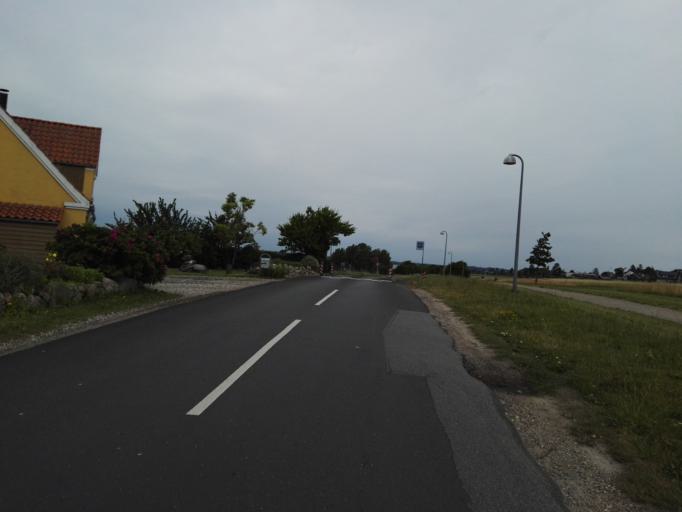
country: DK
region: Zealand
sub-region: Roskilde Kommune
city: Jyllinge
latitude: 55.7559
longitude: 12.1030
